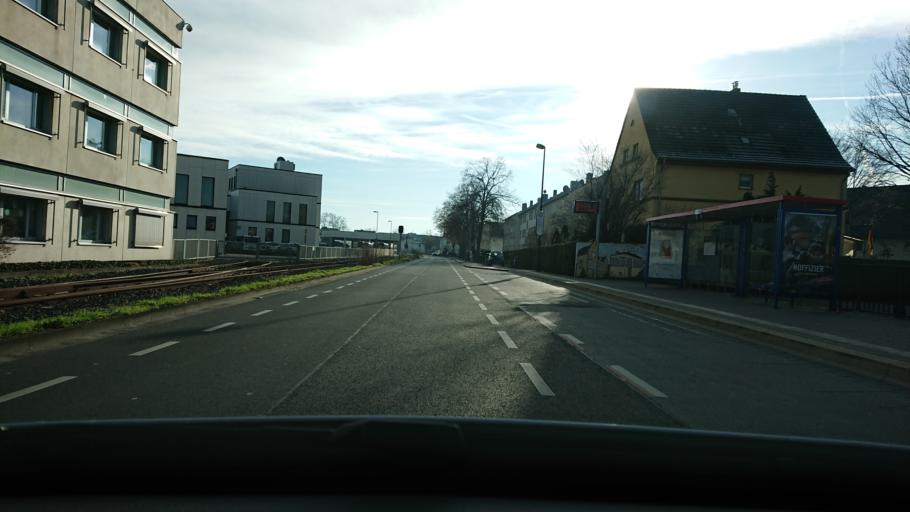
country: DE
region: North Rhine-Westphalia
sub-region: Regierungsbezirk Koln
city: Troisdorf
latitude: 50.8031
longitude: 7.1252
